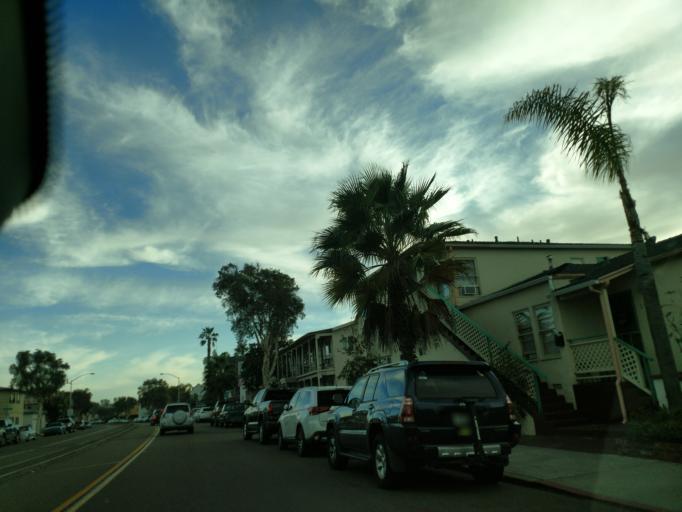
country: US
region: California
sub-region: San Diego County
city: La Jolla
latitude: 32.7646
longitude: -117.2514
